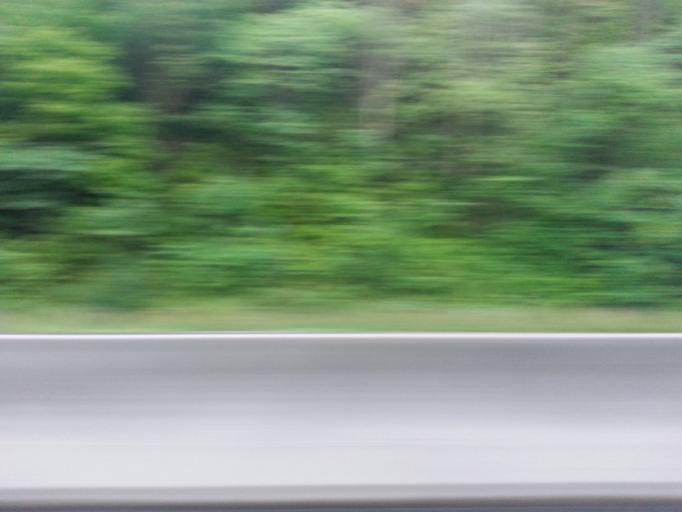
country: US
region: Tennessee
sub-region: Campbell County
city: Jellico
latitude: 36.5599
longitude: -84.1303
